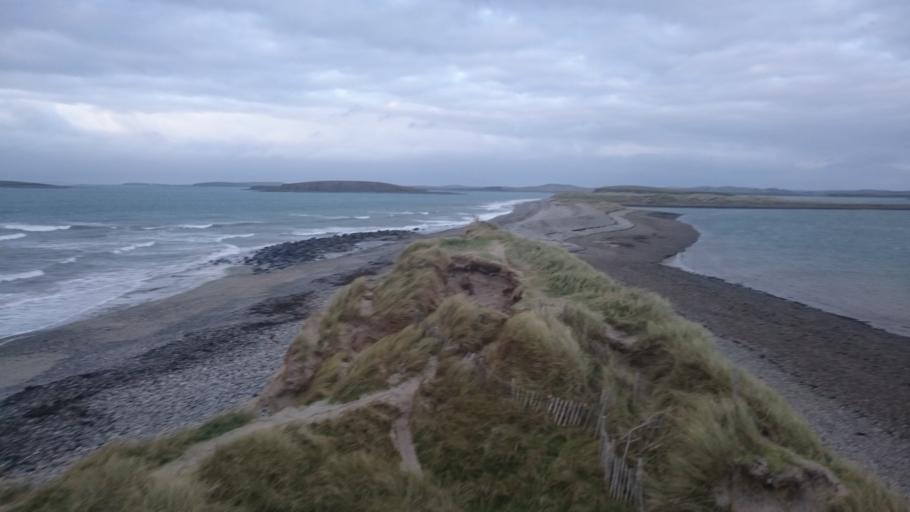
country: IE
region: Connaught
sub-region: Maigh Eo
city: Westport
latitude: 53.7923
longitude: -9.6564
